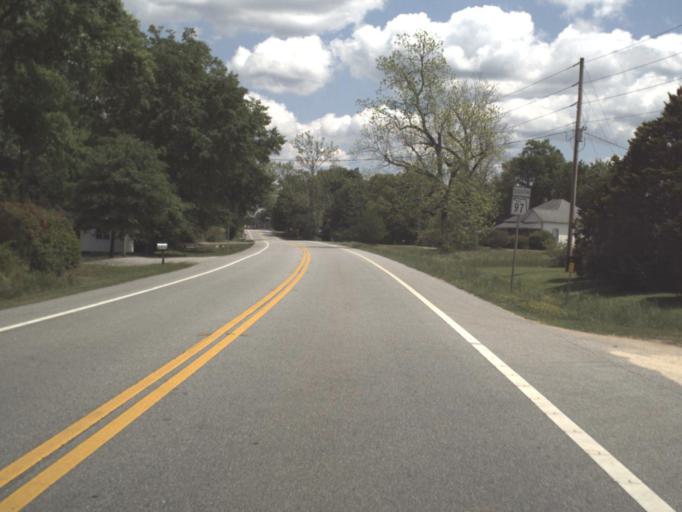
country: US
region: Alabama
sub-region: Escambia County
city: Atmore
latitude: 30.8889
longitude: -87.4625
